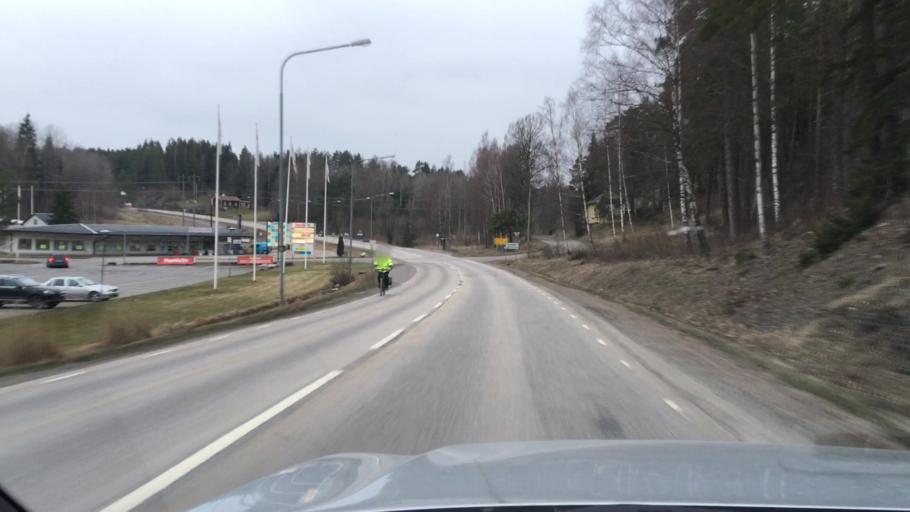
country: SE
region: OEstergoetland
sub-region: Valdemarsviks Kommun
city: Valdemarsvik
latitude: 58.2165
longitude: 16.5787
